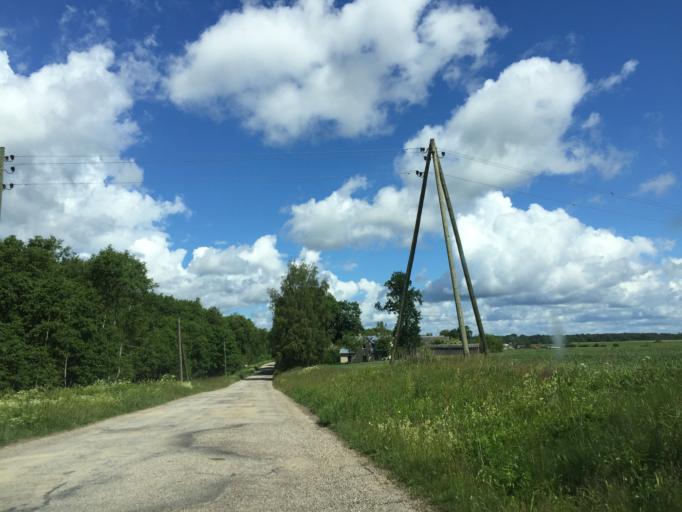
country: LV
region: Lecava
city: Iecava
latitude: 56.6096
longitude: 24.1908
